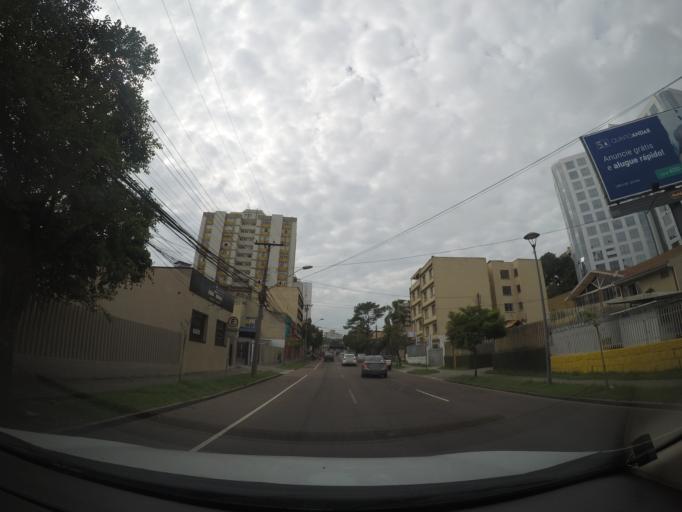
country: BR
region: Parana
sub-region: Curitiba
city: Curitiba
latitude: -25.4190
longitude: -49.2669
